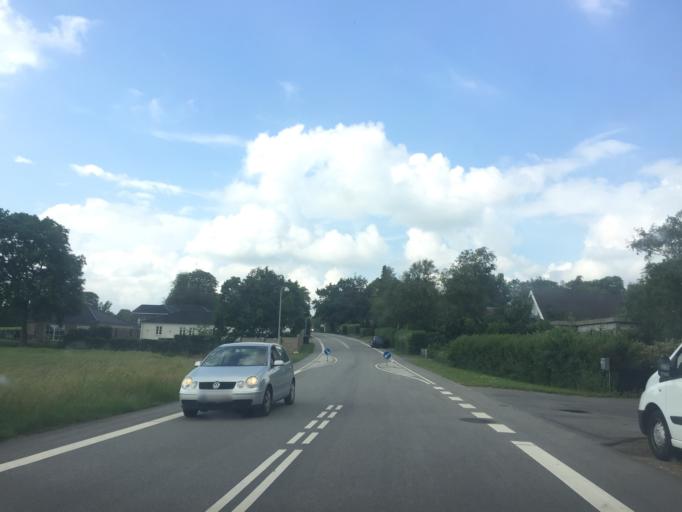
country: DK
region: Zealand
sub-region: Roskilde Kommune
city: Gundsomagle
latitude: 55.7054
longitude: 12.1626
